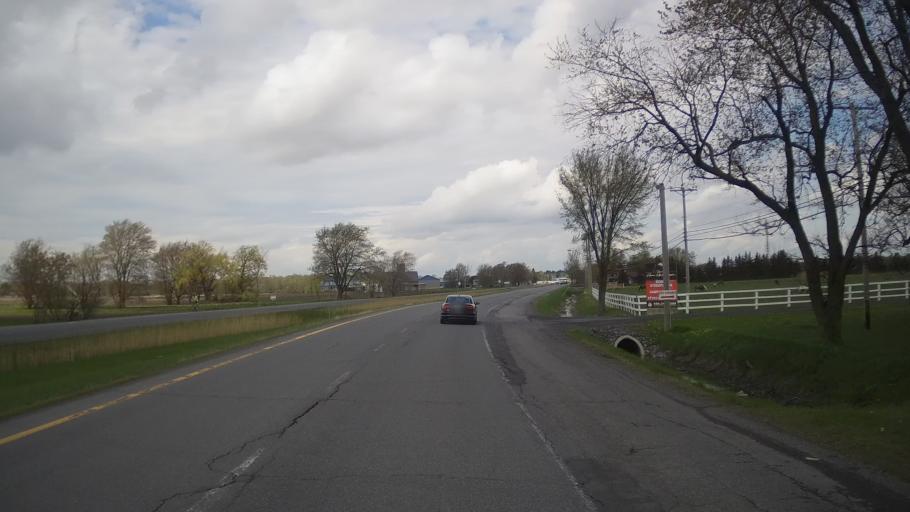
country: CA
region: Quebec
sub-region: Monteregie
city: Carignan
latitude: 45.3704
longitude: -73.3451
